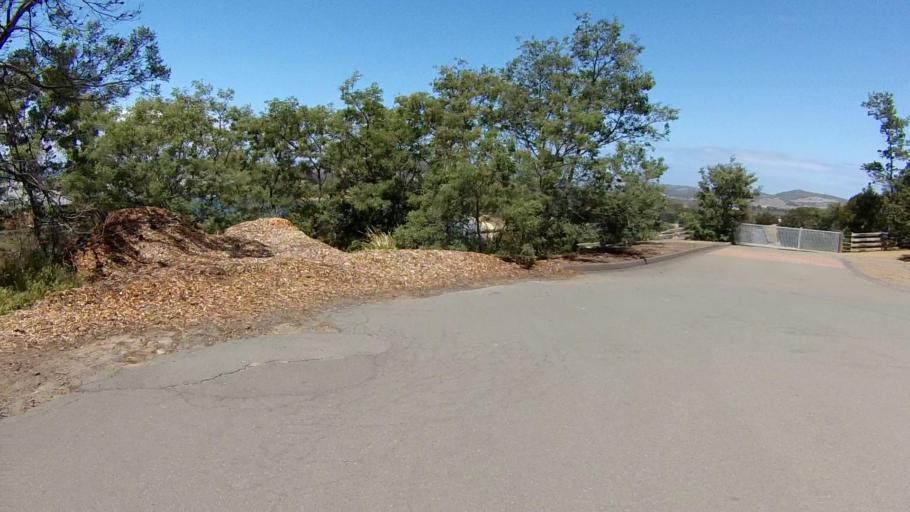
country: AU
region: Tasmania
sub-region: Clarence
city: Sandford
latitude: -42.9187
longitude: 147.5115
